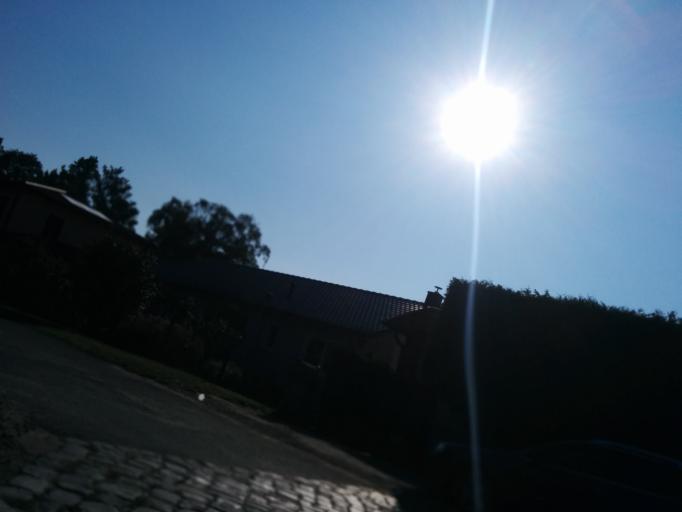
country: DE
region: Berlin
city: Grunau
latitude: 52.4044
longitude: 13.5801
